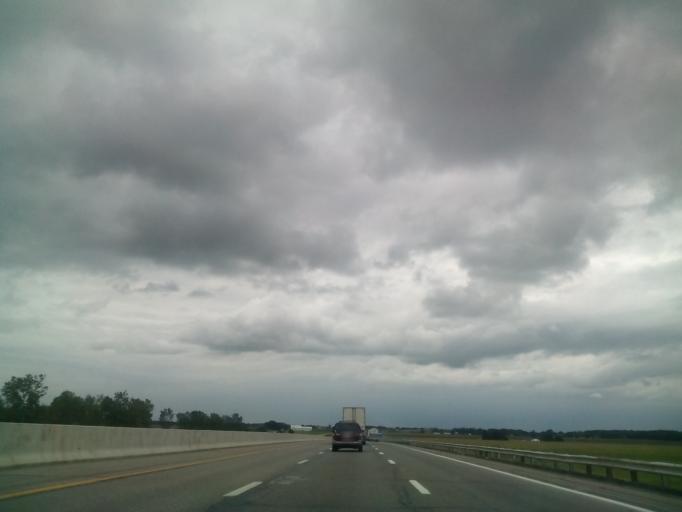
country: US
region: Ohio
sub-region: Wood County
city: Walbridge
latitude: 41.5395
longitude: -83.5090
